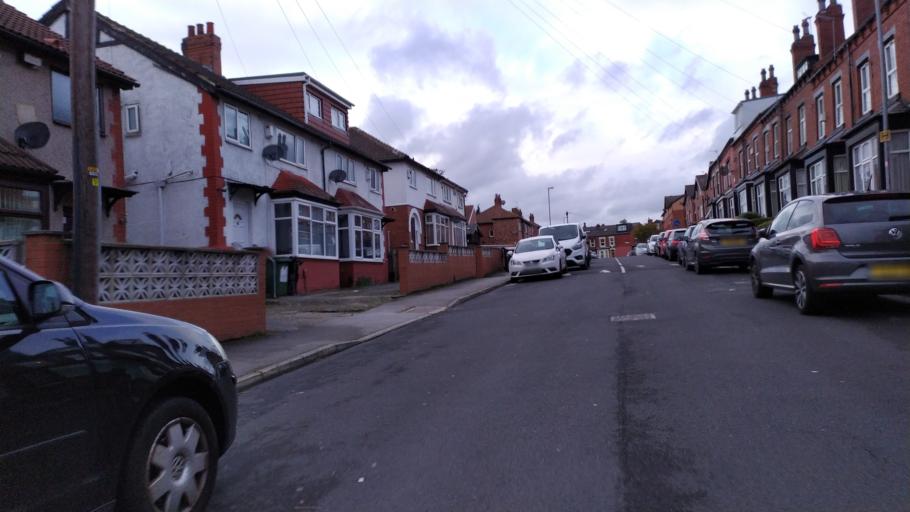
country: GB
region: England
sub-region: City and Borough of Leeds
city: Leeds
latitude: 53.8118
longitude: -1.5722
